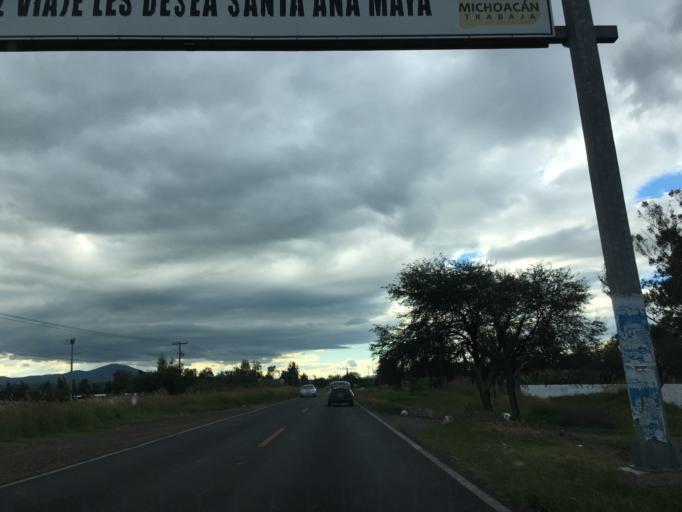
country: MX
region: Michoacan
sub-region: Cuitzeo
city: Cuamio
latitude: 20.0743
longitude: -101.1281
